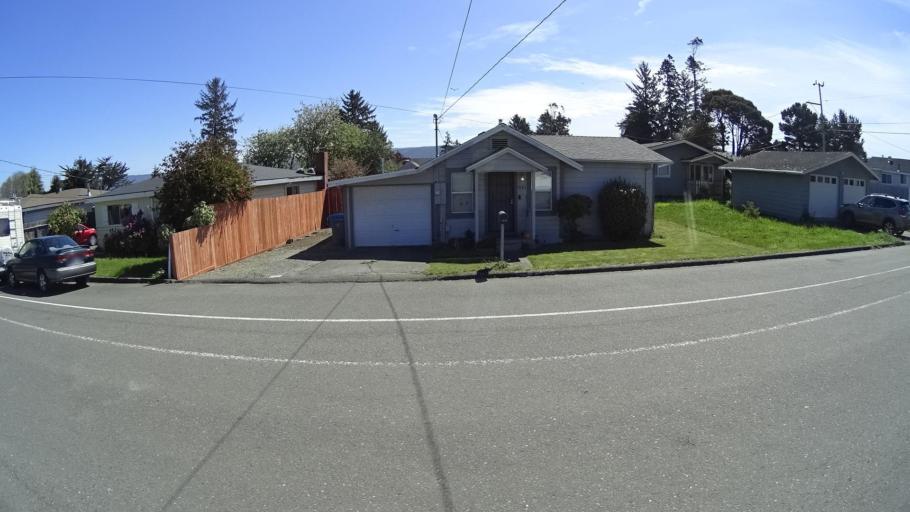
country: US
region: California
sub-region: Humboldt County
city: Myrtletown
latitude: 40.7942
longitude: -124.1264
